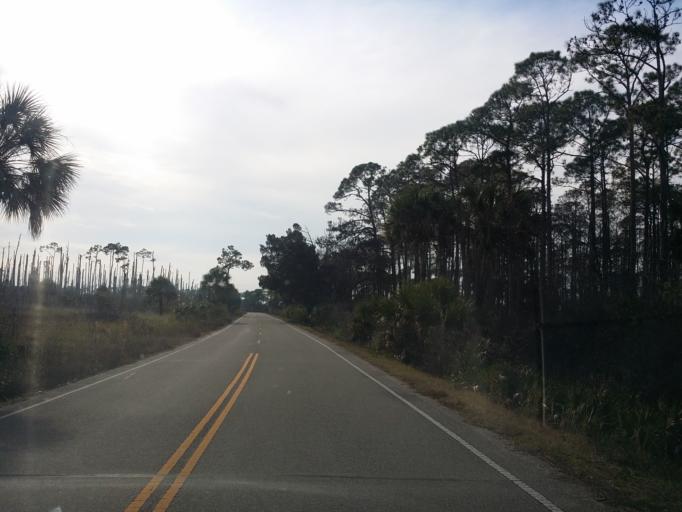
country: US
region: Florida
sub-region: Wakulla County
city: Crawfordville
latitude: 30.0965
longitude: -84.1626
